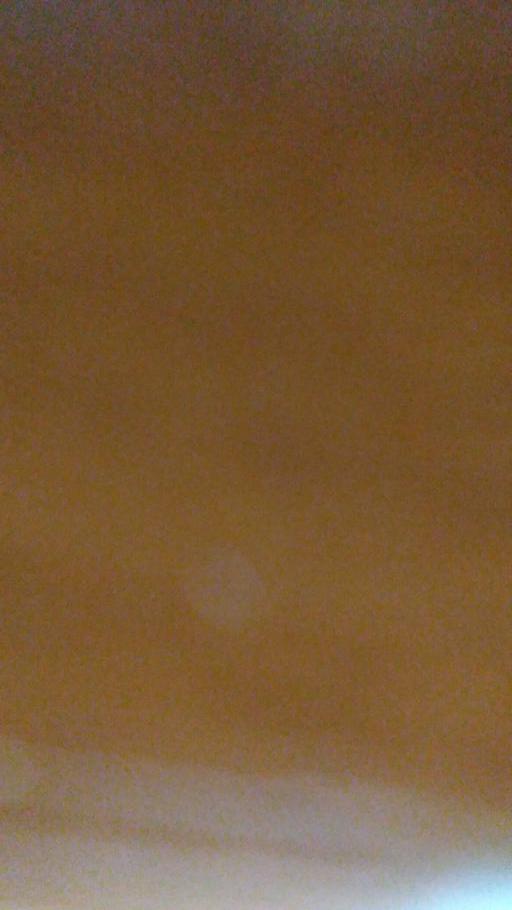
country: RU
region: Tula
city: Volovo
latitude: 53.5937
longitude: 38.1051
